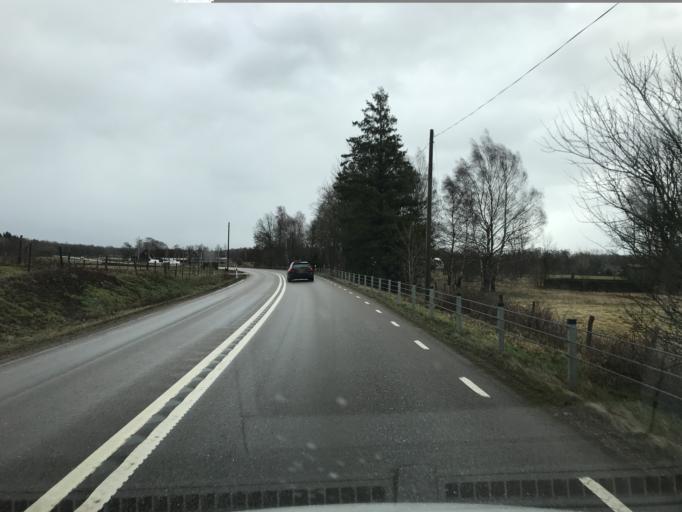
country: SE
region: Skane
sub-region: Klippans Kommun
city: Ljungbyhed
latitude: 56.0968
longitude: 13.1849
